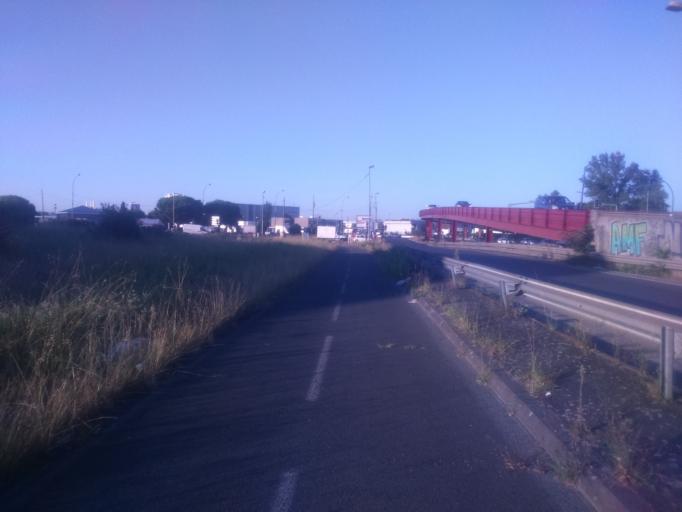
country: FR
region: Aquitaine
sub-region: Departement de la Gironde
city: Le Bouscat
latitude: 44.8713
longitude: -0.5659
